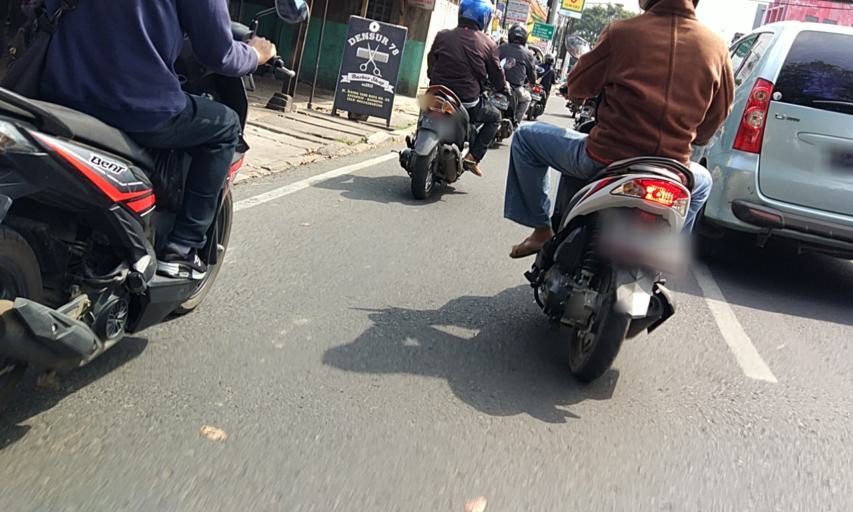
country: ID
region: West Java
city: Bandung
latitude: -6.9049
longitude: 107.6782
